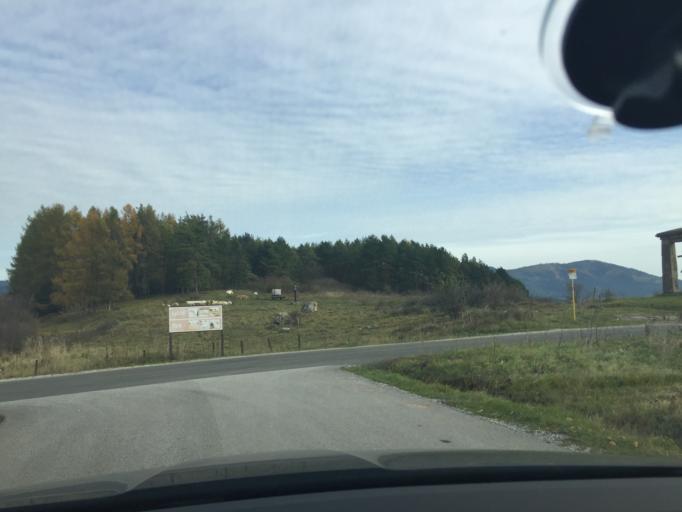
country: SK
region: Presovsky
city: Spisske Podhradie
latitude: 48.9987
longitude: 20.7788
